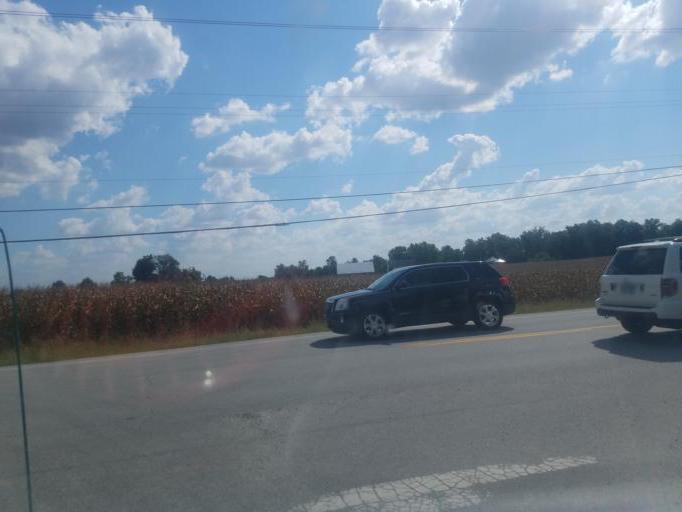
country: US
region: Ohio
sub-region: Auglaize County
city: Saint Marys
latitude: 40.5860
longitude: -84.3176
